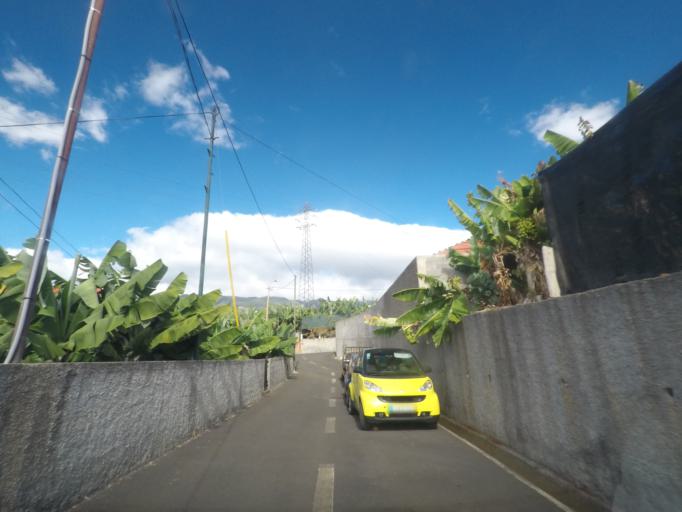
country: PT
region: Madeira
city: Camara de Lobos
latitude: 32.6521
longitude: -16.9580
